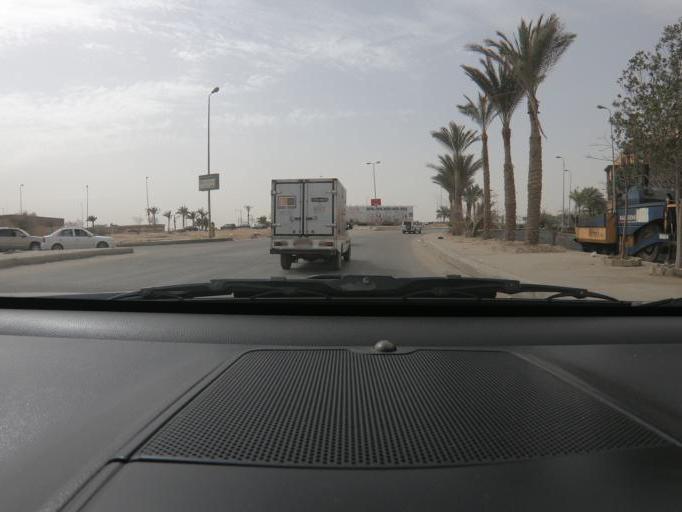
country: EG
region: Muhafazat al Qahirah
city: Cairo
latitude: 30.0217
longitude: 31.4122
